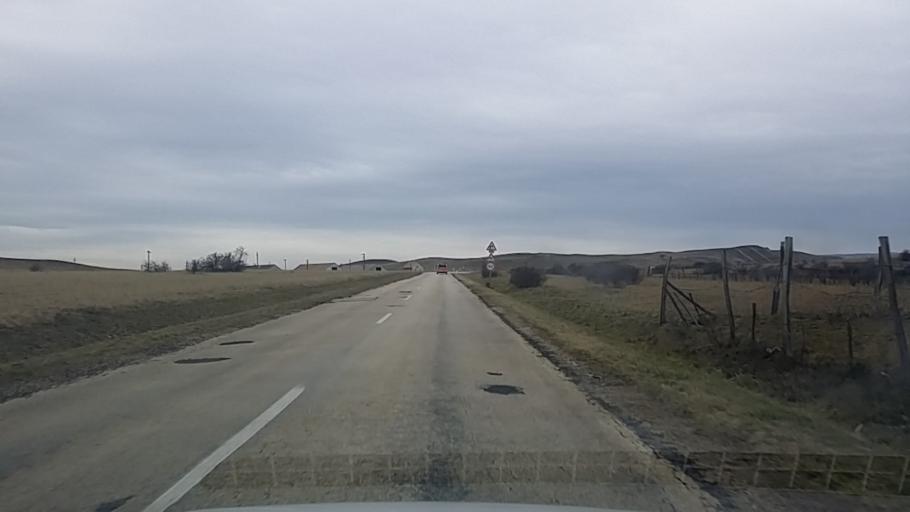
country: HU
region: Fejer
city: Zamoly
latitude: 47.3403
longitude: 18.3608
